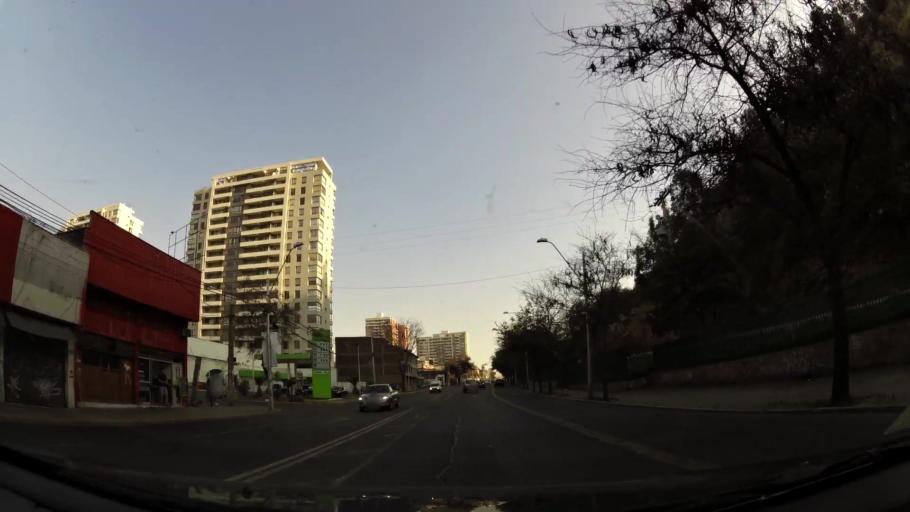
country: CL
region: Santiago Metropolitan
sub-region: Provincia de Santiago
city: Santiago
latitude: -33.4192
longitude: -70.6441
